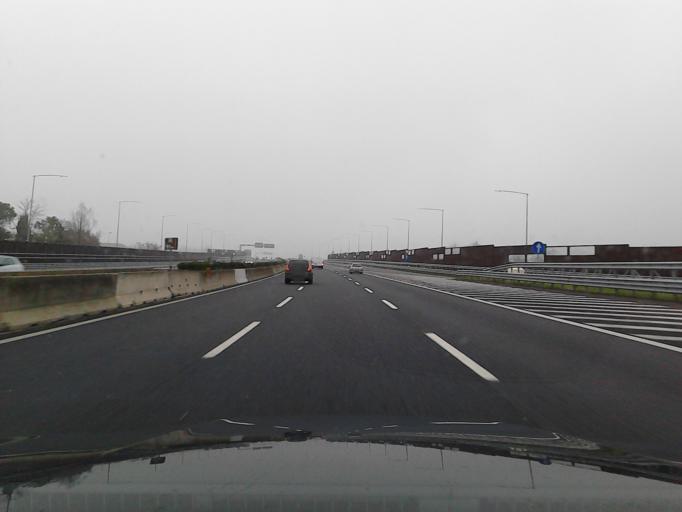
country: IT
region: Emilia-Romagna
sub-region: Forli-Cesena
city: Gatteo-Sant'Angelo
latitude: 44.1198
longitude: 12.3933
